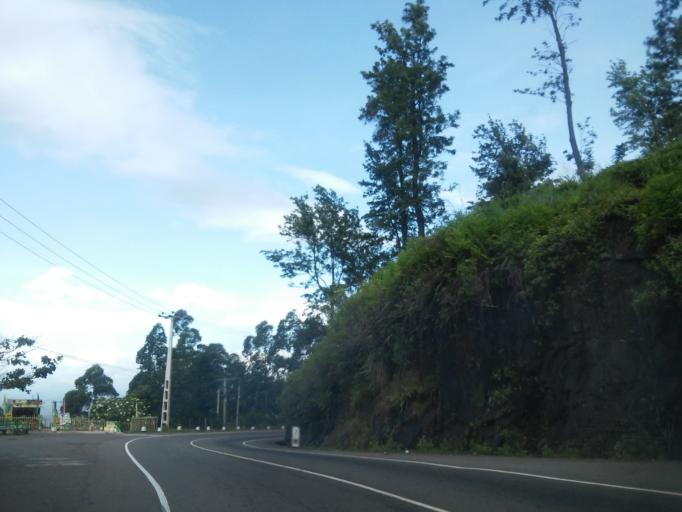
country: LK
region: Uva
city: Haputale
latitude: 6.7617
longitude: 80.9301
